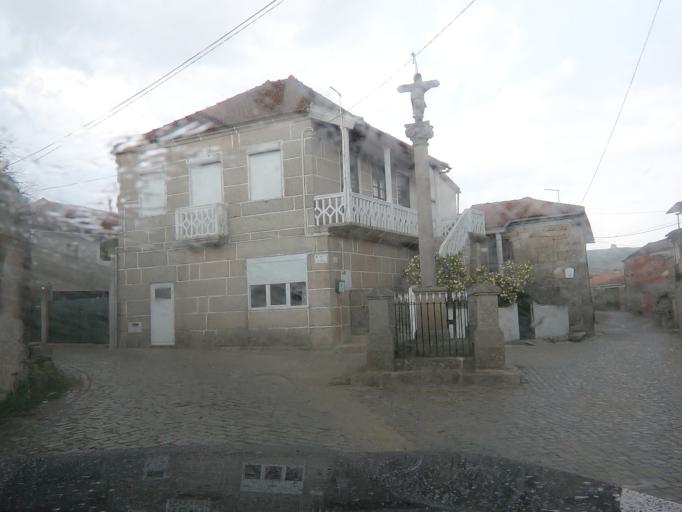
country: PT
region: Vila Real
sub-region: Vila Real
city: Vila Real
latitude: 41.3568
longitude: -7.6987
